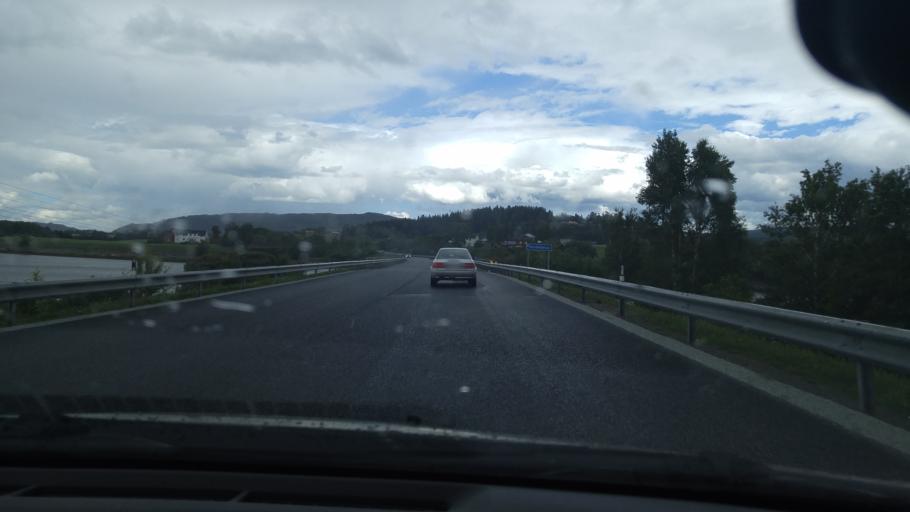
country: NO
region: Nord-Trondelag
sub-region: Verdal
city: Verdal
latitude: 63.8019
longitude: 11.4594
